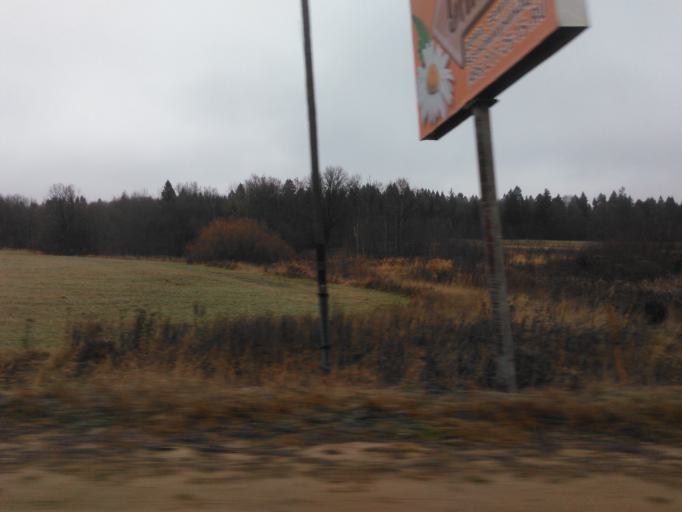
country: RU
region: Moskovskaya
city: Muranovo
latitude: 56.1781
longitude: 37.9117
